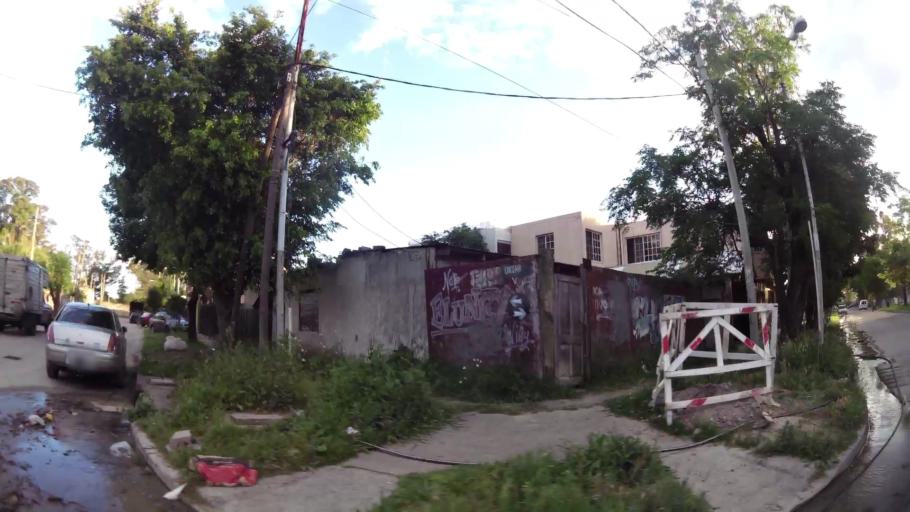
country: AR
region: Buenos Aires
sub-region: Partido de Avellaneda
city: Avellaneda
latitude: -34.7040
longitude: -58.3398
